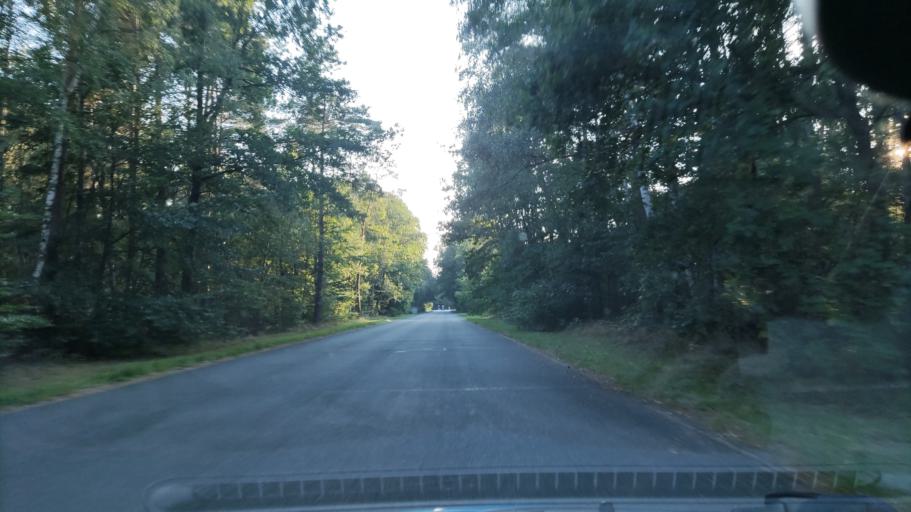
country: DE
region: Lower Saxony
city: Munster
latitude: 52.9758
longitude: 10.1506
